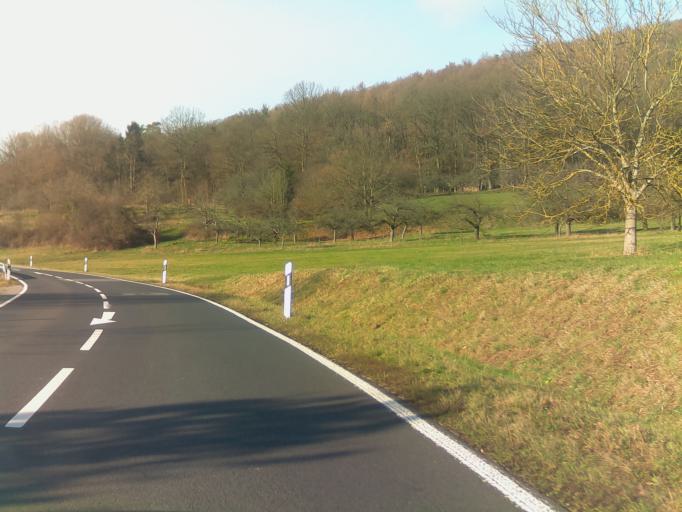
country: DE
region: Baden-Wuerttemberg
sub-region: Regierungsbezirk Stuttgart
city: Freudenberg
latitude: 49.7772
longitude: 9.3295
